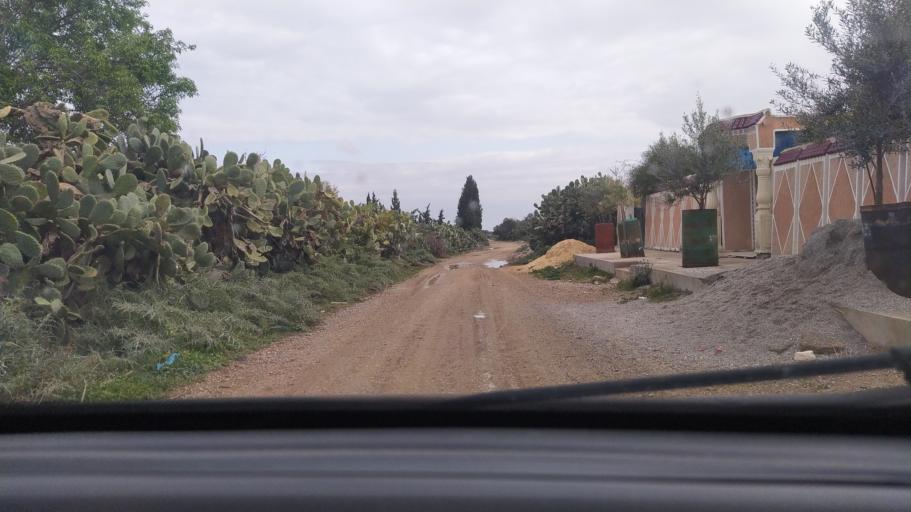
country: TN
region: Al Munastir
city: Sidi Bin Nur
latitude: 35.5171
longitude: 10.9294
